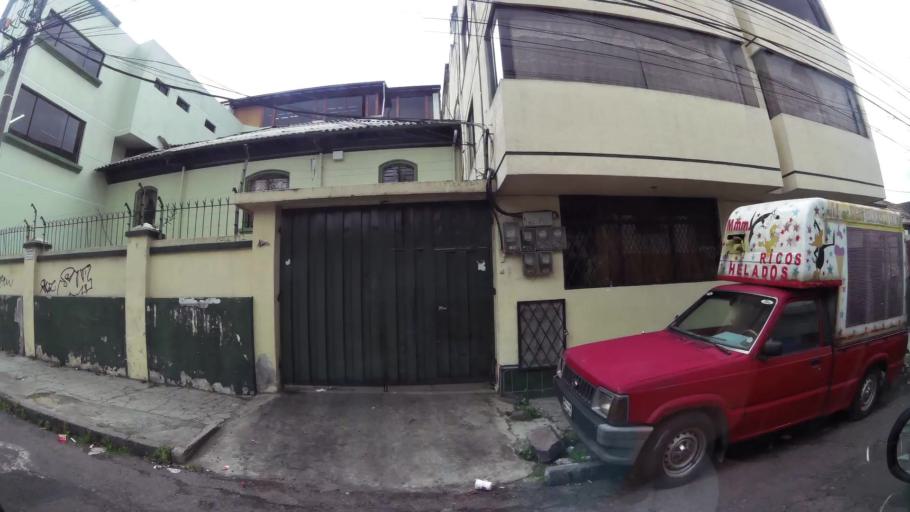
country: EC
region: Pichincha
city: Quito
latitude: -0.2426
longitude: -78.5254
